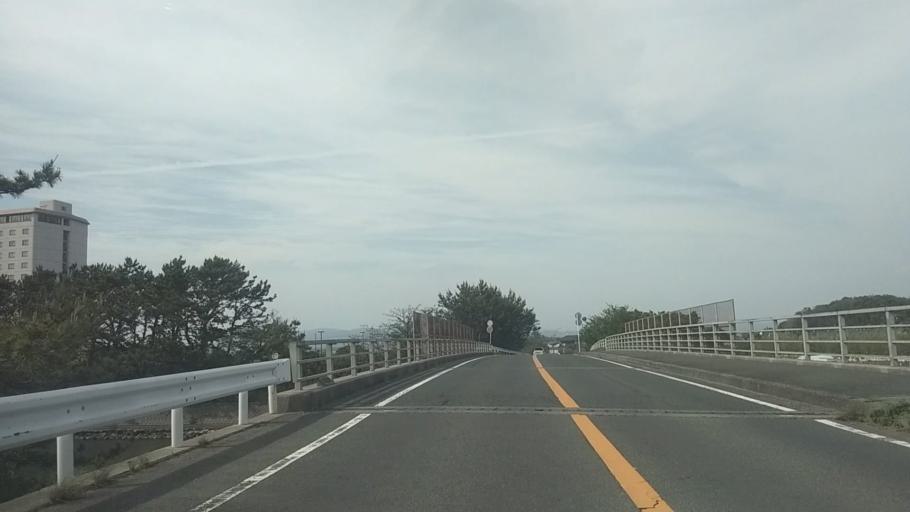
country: JP
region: Shizuoka
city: Kosai-shi
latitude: 34.7050
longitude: 137.6171
